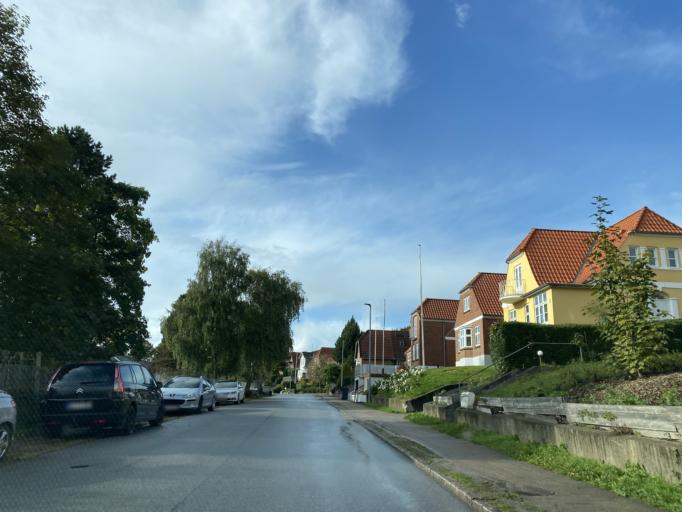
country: DK
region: South Denmark
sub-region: Haderslev Kommune
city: Haderslev
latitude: 55.2564
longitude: 9.4906
